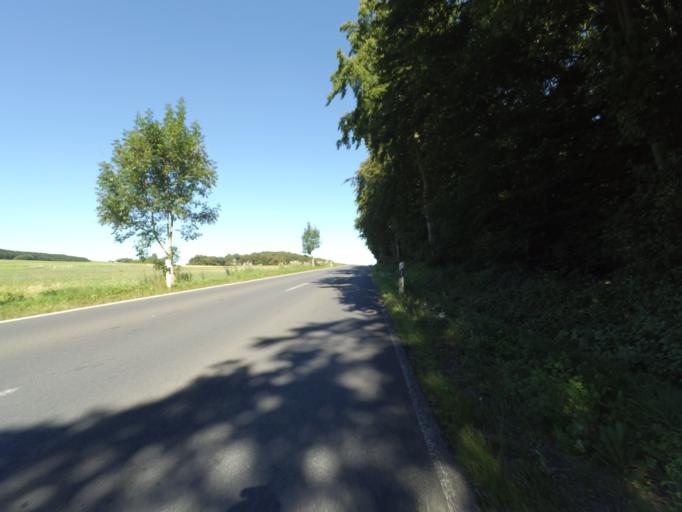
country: DE
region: Rheinland-Pfalz
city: Uxheim
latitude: 50.3261
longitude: 6.7365
